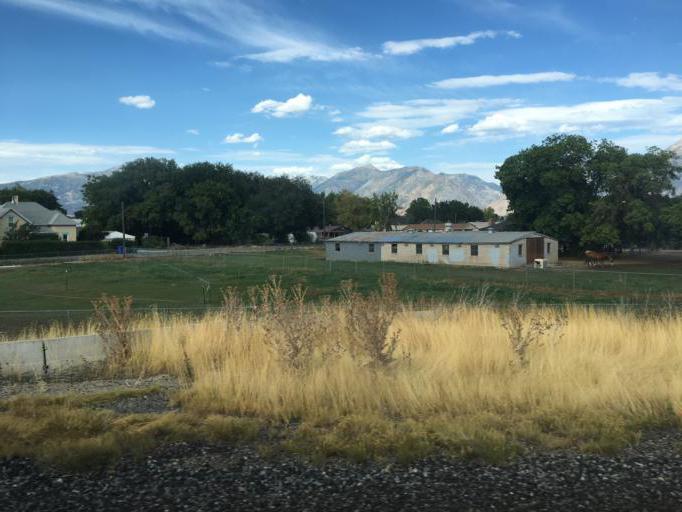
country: US
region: Utah
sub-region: Utah County
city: Lehi
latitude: 40.3823
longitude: -111.8539
